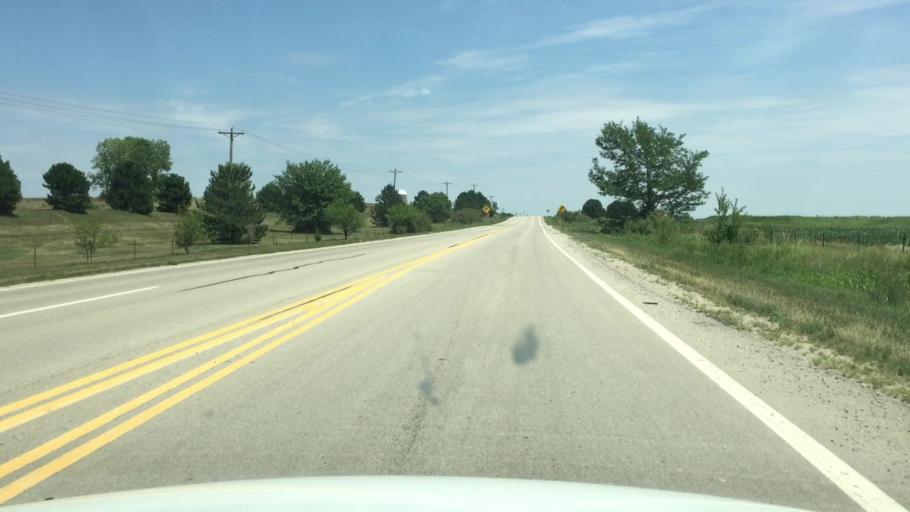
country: US
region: Kansas
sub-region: Shawnee County
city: Topeka
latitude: 38.9859
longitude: -95.4992
